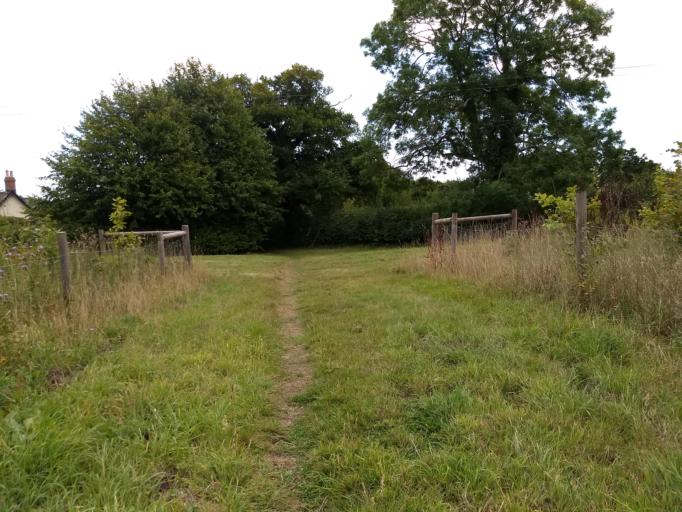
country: GB
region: England
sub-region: Isle of Wight
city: Ryde
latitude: 50.7073
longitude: -1.1825
